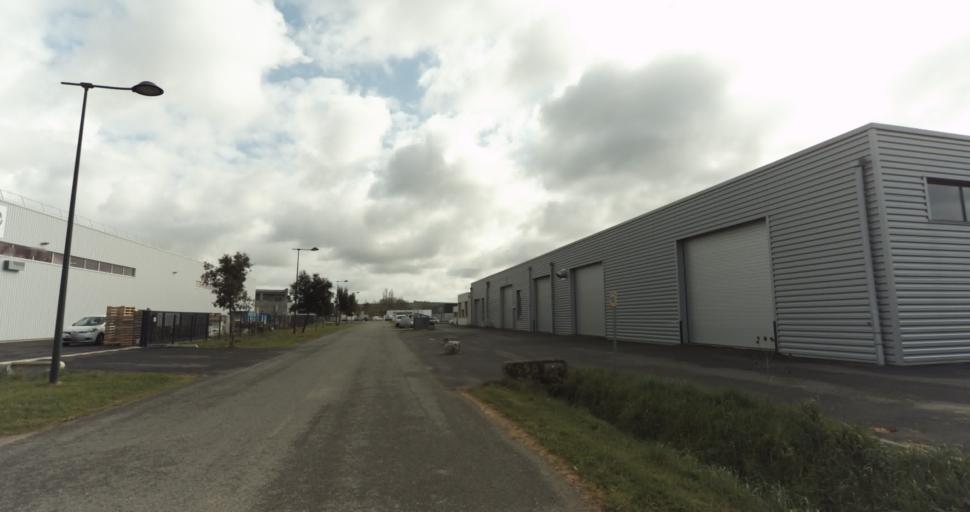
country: FR
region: Midi-Pyrenees
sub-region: Departement de la Haute-Garonne
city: Auterive
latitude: 43.3627
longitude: 1.4517
